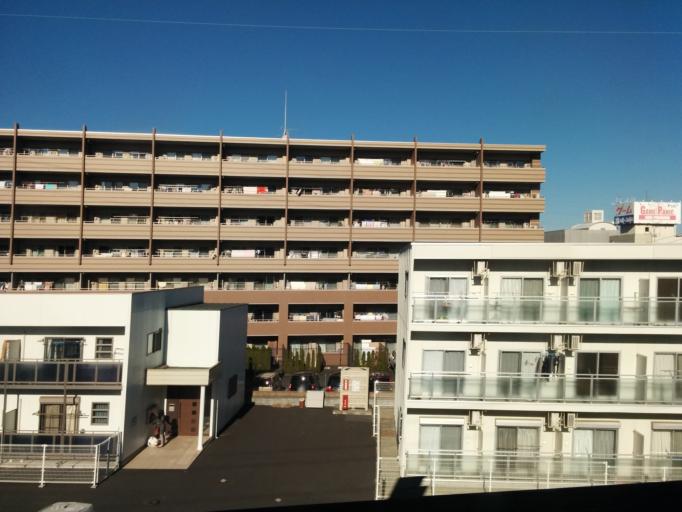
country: JP
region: Kanagawa
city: Yokohama
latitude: 35.5129
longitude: 139.6242
